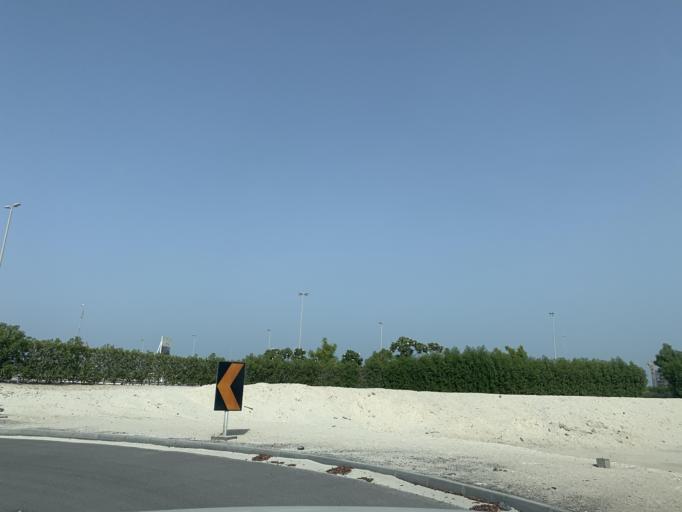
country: BH
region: Muharraq
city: Al Muharraq
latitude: 26.3119
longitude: 50.6404
